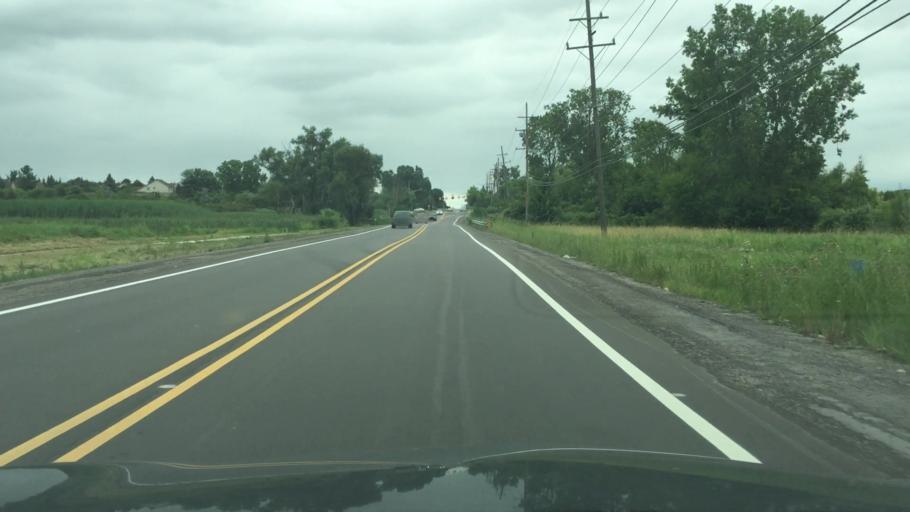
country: US
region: Michigan
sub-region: Oakland County
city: Walled Lake
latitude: 42.5150
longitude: -83.4371
